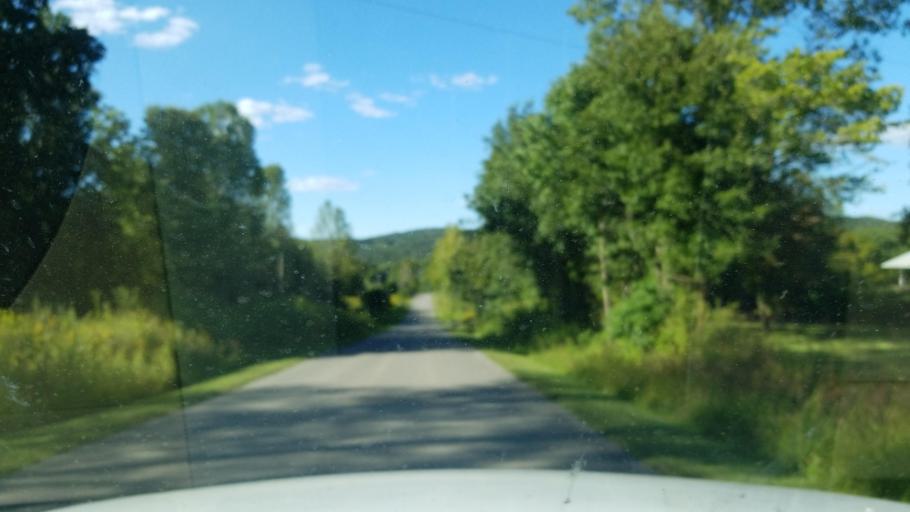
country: US
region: Illinois
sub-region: Hardin County
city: Elizabethtown
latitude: 37.5846
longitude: -88.3655
